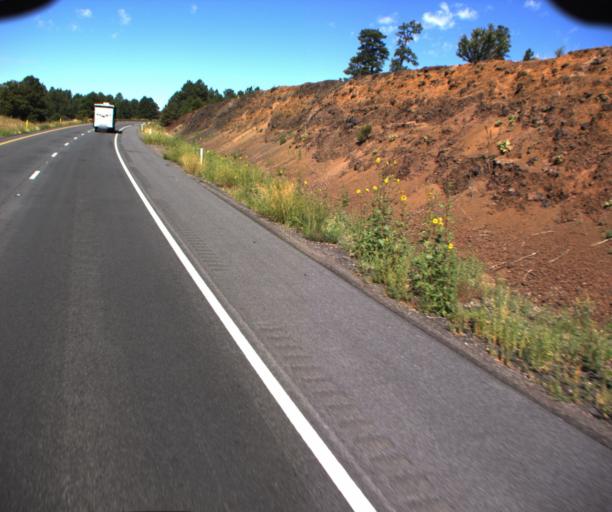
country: US
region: Arizona
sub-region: Coconino County
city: Williams
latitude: 35.2200
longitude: -112.3043
